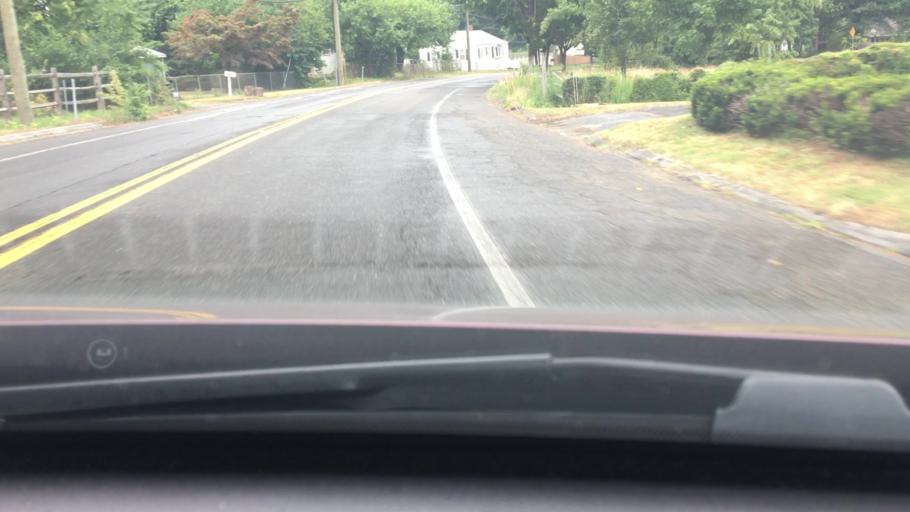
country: US
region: Maryland
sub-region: Prince George's County
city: Beltsville
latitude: 39.0437
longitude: -76.9122
